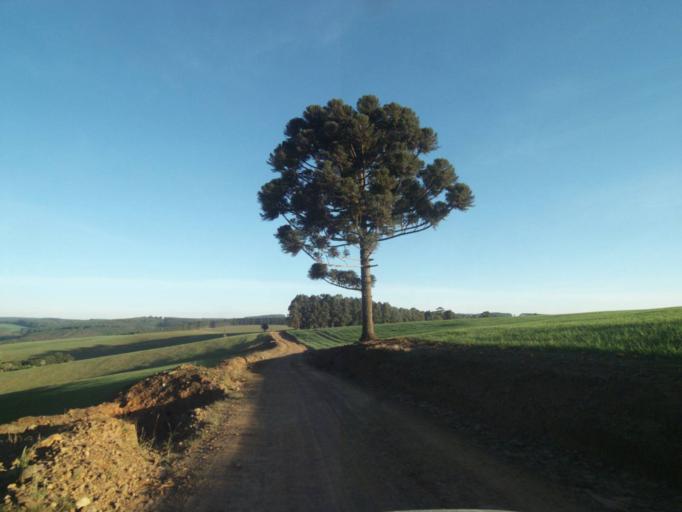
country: BR
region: Parana
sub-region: Telemaco Borba
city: Telemaco Borba
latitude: -24.4740
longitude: -50.5872
